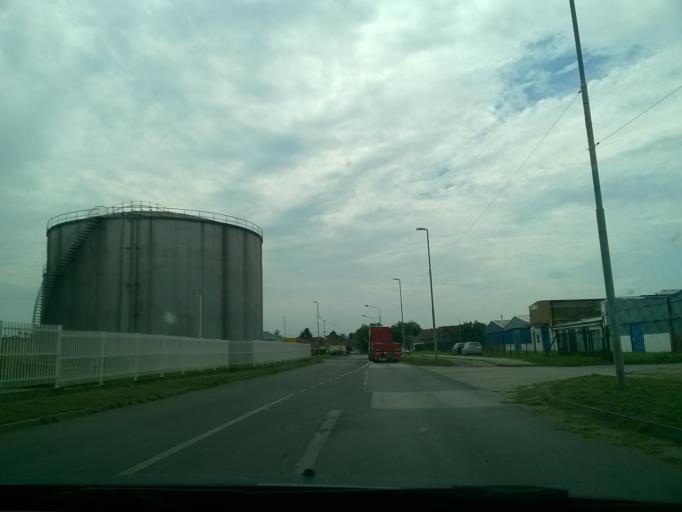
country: RS
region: Autonomna Pokrajina Vojvodina
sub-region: Srednjebanatski Okrug
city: Zrenjanin
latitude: 45.3840
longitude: 20.4151
